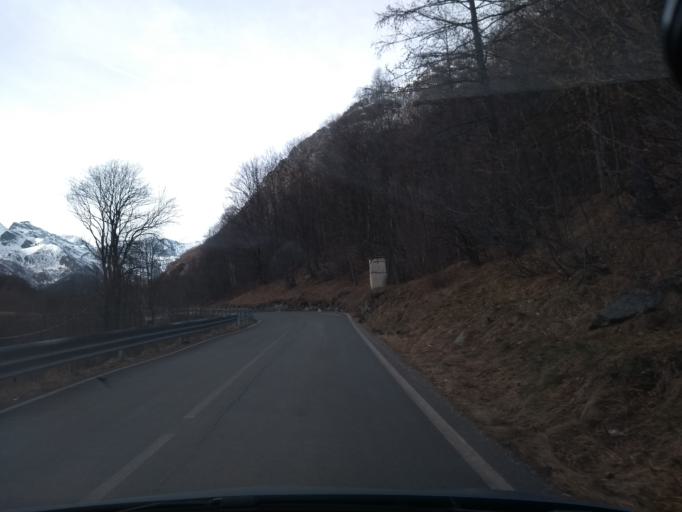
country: IT
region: Piedmont
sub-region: Provincia di Torino
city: Balme
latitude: 45.3110
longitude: 7.2545
